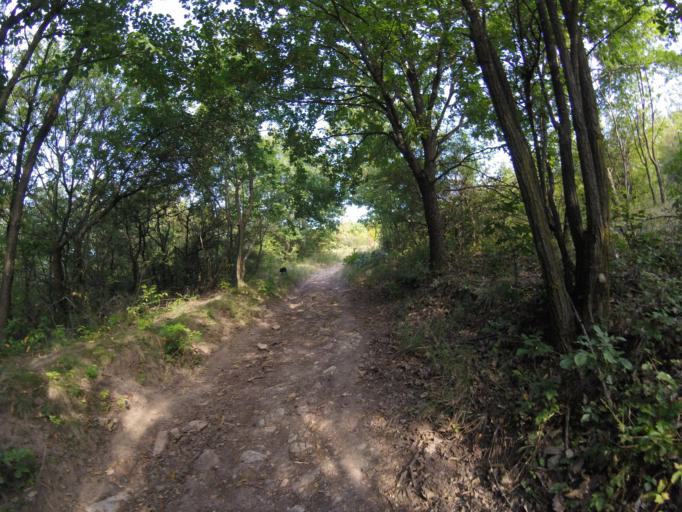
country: HU
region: Pest
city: Pilisszentkereszt
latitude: 47.6983
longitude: 18.9019
